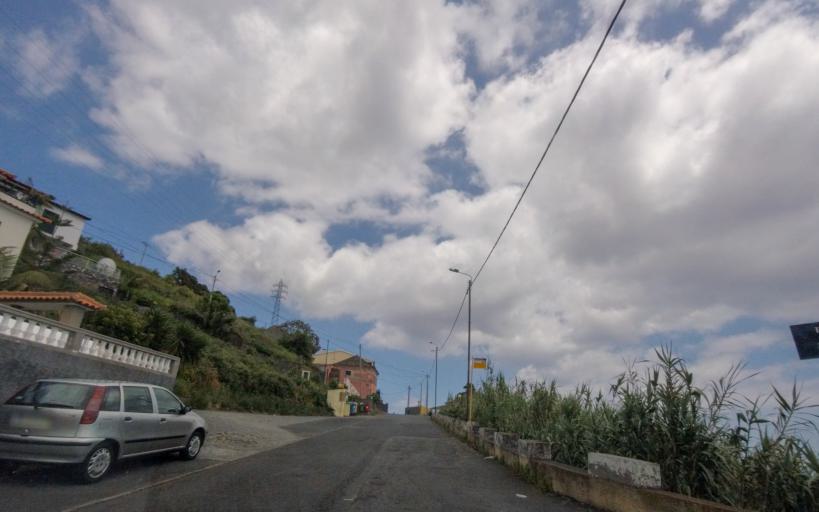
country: PT
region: Madeira
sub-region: Funchal
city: Nossa Senhora do Monte
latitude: 32.6632
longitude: -16.8807
